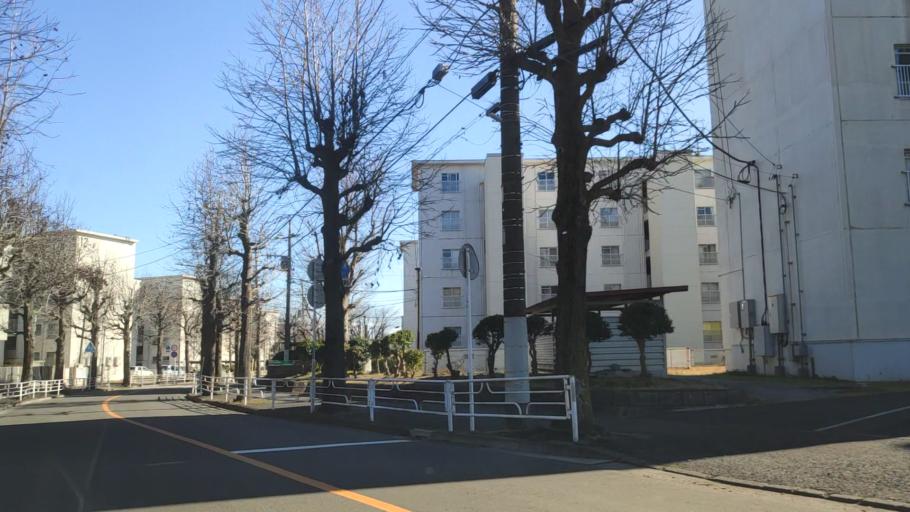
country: JP
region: Kanagawa
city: Minami-rinkan
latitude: 35.5003
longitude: 139.5313
